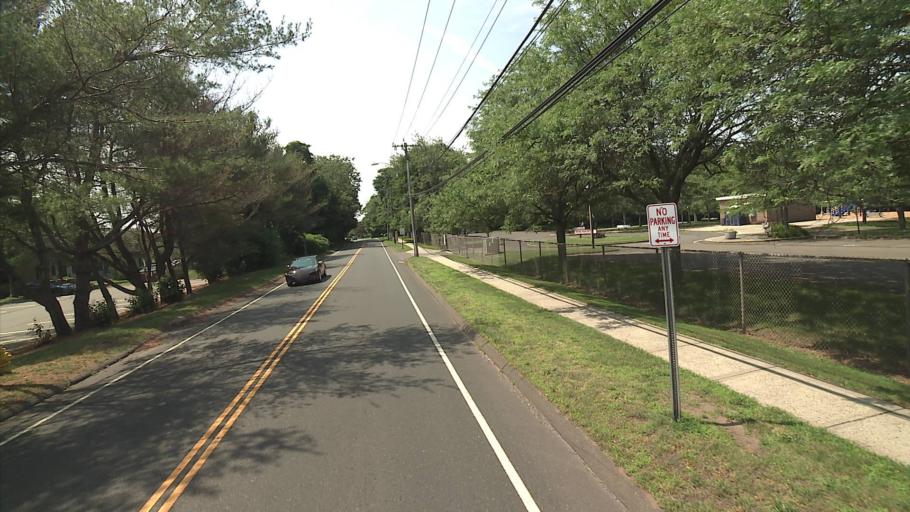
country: US
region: Connecticut
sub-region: New Haven County
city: Branford
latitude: 41.2983
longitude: -72.8199
